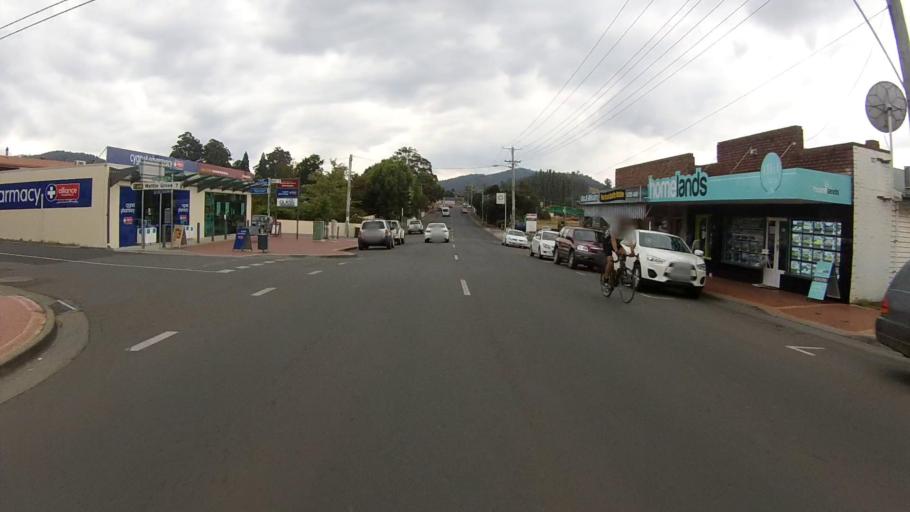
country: AU
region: Tasmania
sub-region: Huon Valley
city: Cygnet
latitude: -43.1607
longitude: 147.0761
